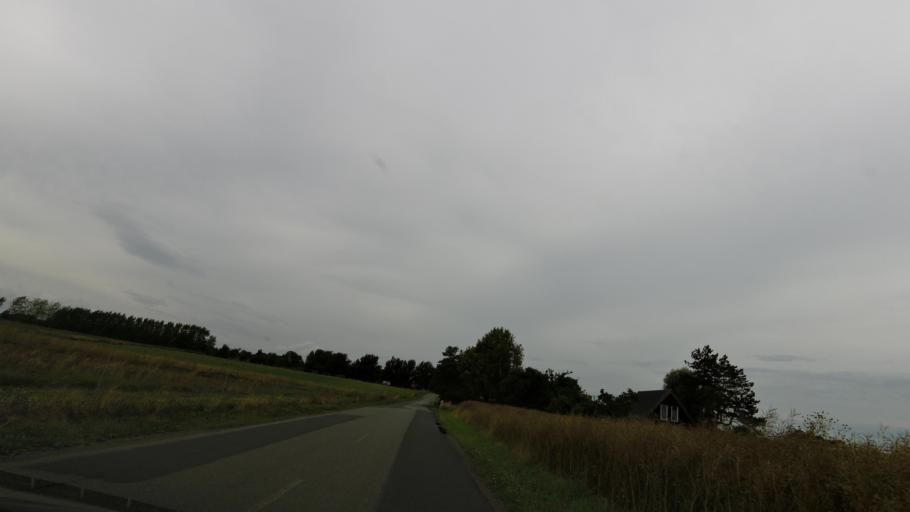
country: DK
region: South Denmark
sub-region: Nordfyns Kommune
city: Otterup
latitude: 55.5791
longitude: 10.3947
